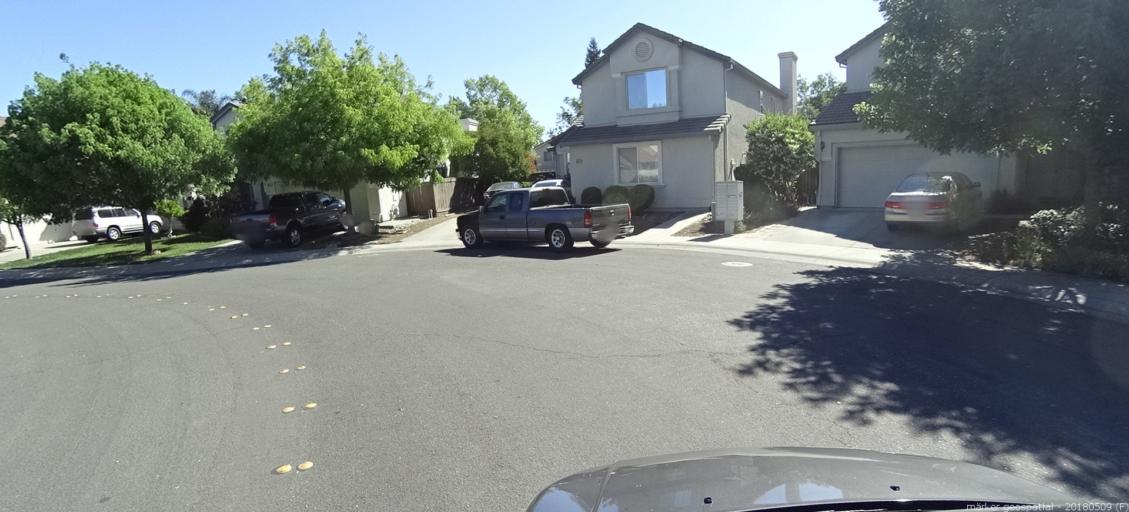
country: US
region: California
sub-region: Sacramento County
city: Elverta
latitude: 38.6690
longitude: -121.5181
